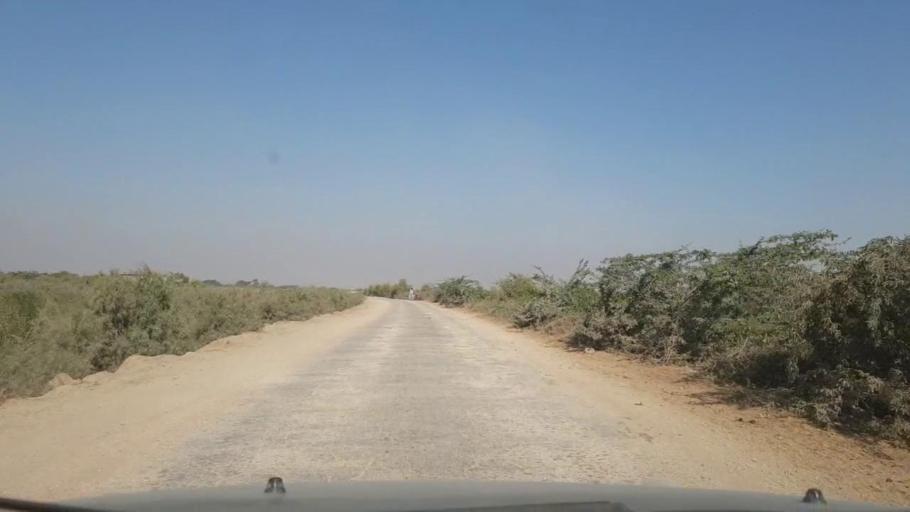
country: PK
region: Sindh
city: Thatta
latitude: 24.8050
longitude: 67.9014
